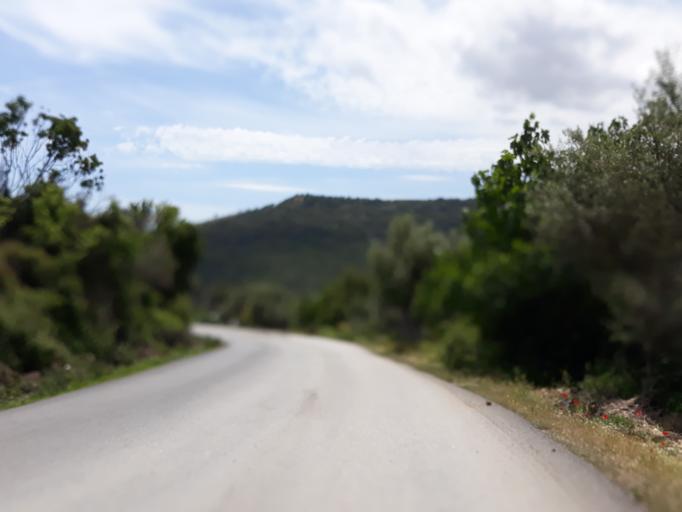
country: GR
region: Attica
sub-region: Nomarchia Dytikis Attikis
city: Magoula
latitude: 38.1465
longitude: 23.5245
